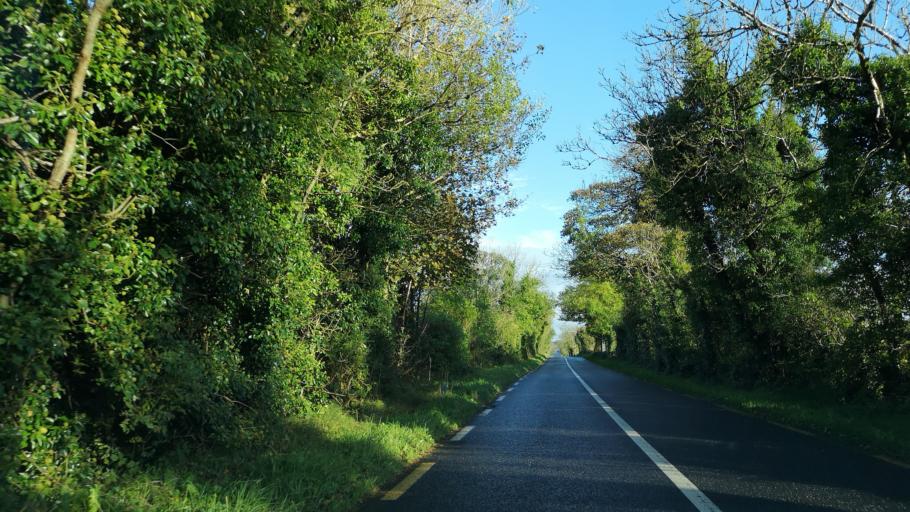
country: IE
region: Connaught
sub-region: Roscommon
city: Castlerea
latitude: 53.8205
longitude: -8.5468
